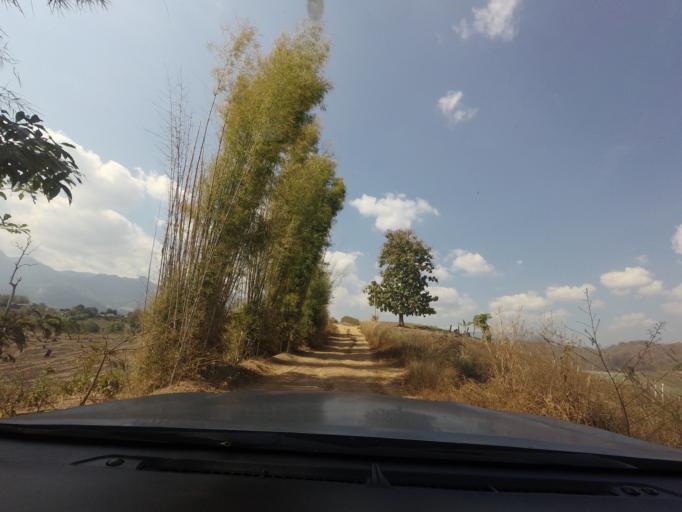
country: TH
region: Mae Hong Son
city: Wiang Nuea
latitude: 19.4000
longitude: 98.4109
